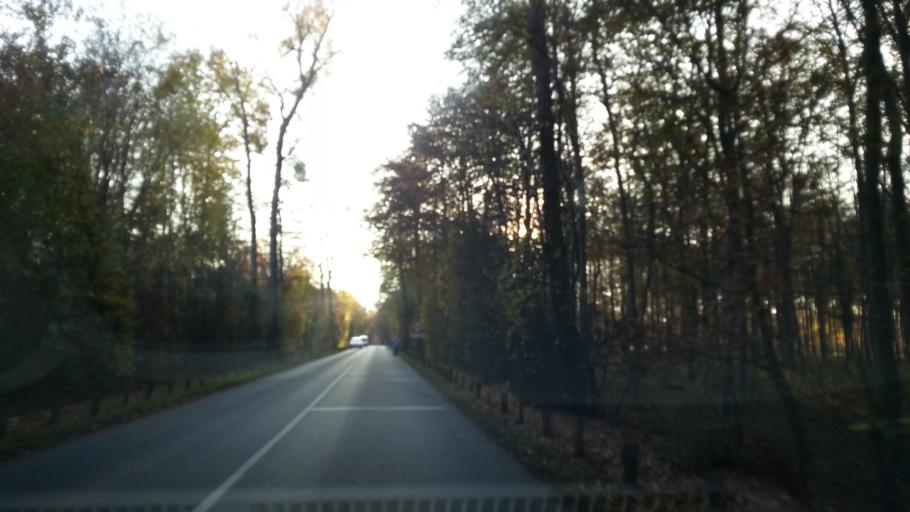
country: FR
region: Picardie
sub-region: Departement de l'Oise
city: Chantilly
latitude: 49.1888
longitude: 2.4795
